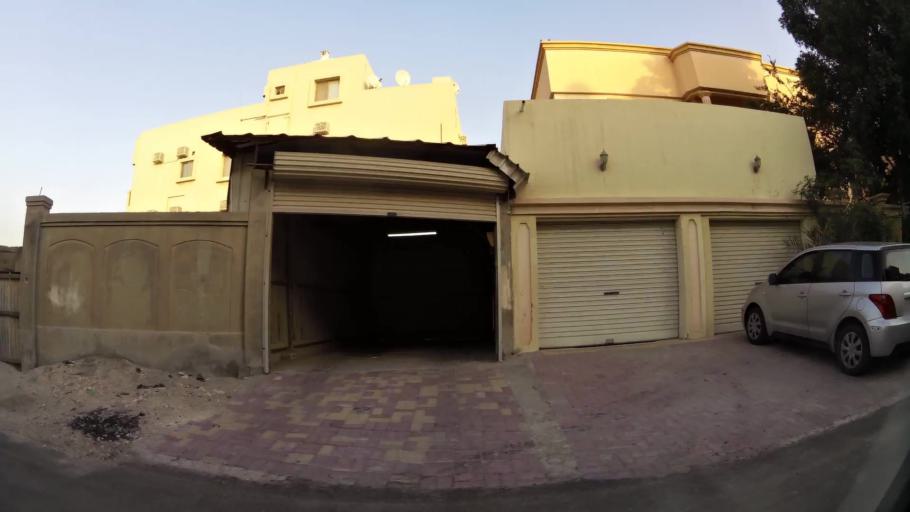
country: BH
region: Northern
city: Madinat `Isa
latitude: 26.1850
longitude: 50.4758
